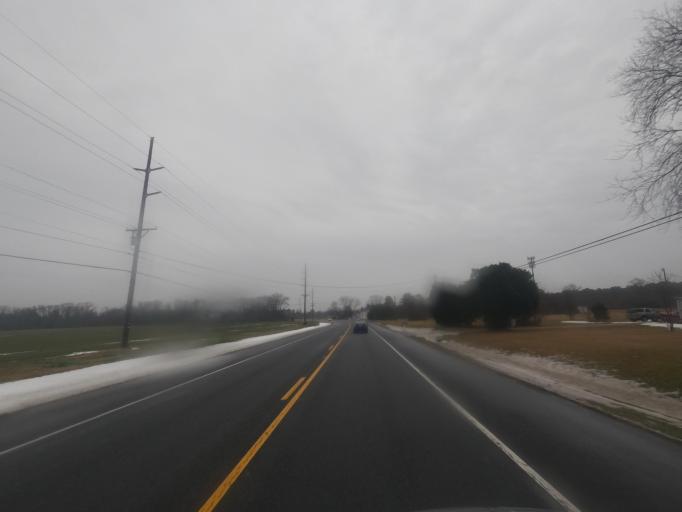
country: US
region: Maryland
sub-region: Dorchester County
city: Cambridge
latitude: 38.5818
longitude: -75.9648
